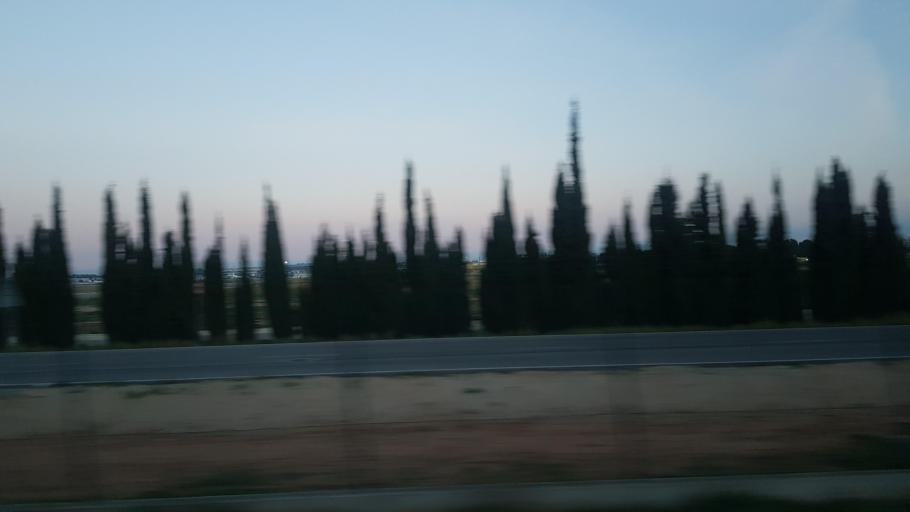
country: ES
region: Valencia
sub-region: Provincia de Valencia
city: Manises
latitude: 39.4806
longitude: -0.4651
